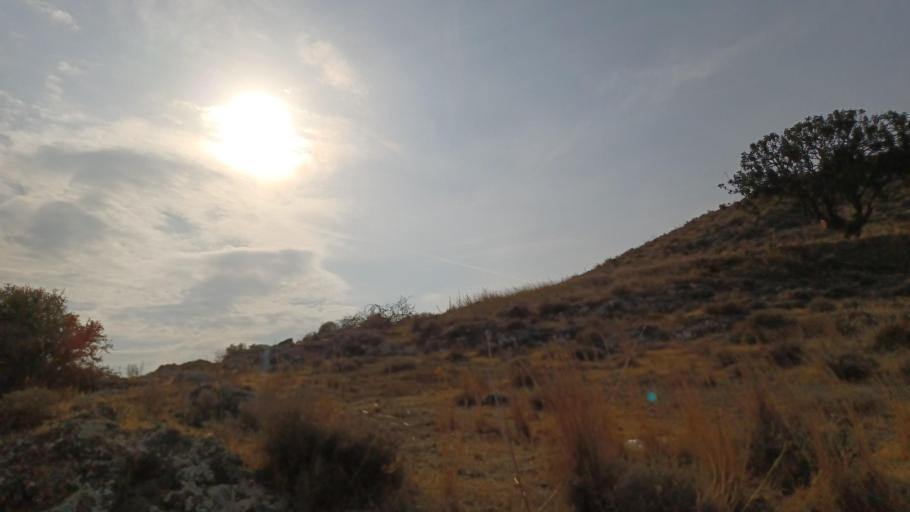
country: CY
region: Larnaka
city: Troulloi
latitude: 35.0247
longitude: 33.6099
